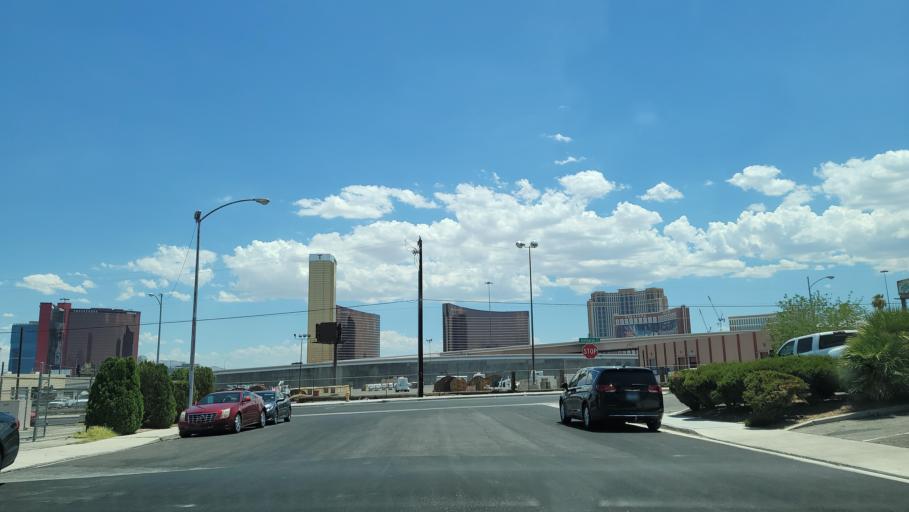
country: US
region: Nevada
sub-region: Clark County
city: Paradise
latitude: 36.1287
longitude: -115.1838
